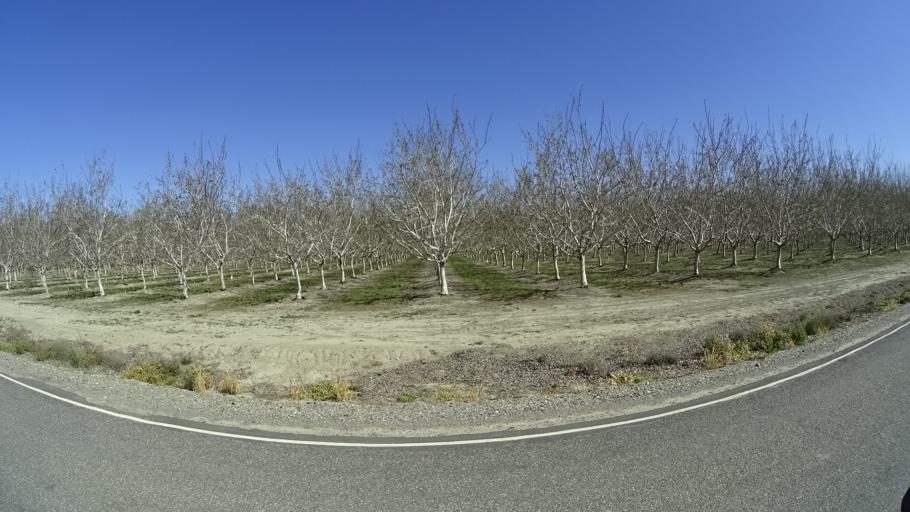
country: US
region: California
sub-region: Glenn County
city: Willows
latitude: 39.6235
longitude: -122.1100
